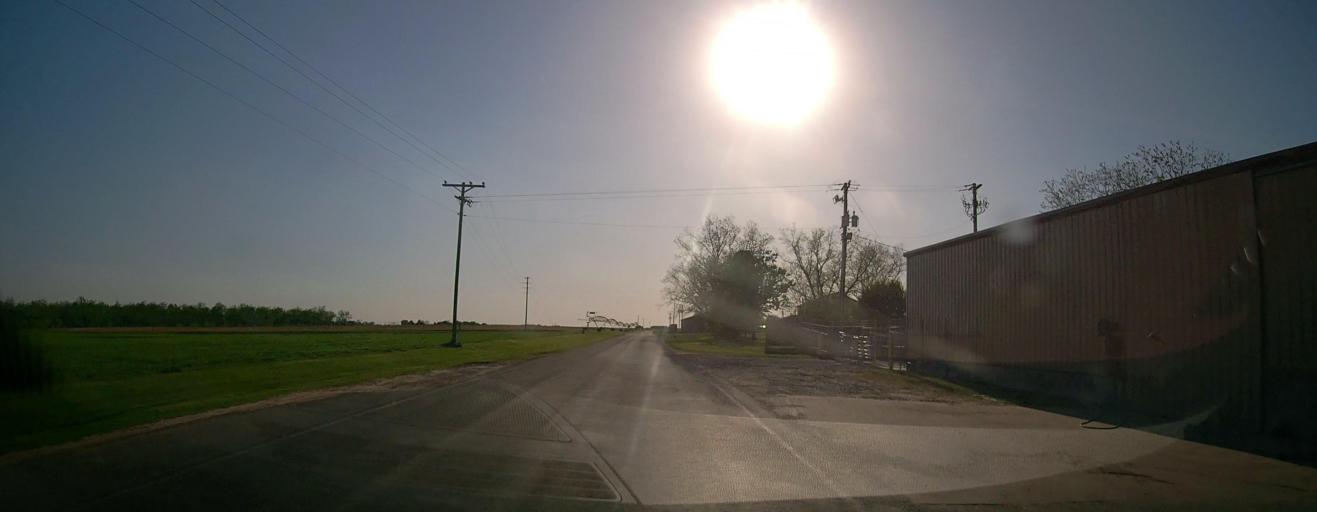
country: US
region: Georgia
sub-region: Macon County
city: Montezuma
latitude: 32.3187
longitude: -83.9710
